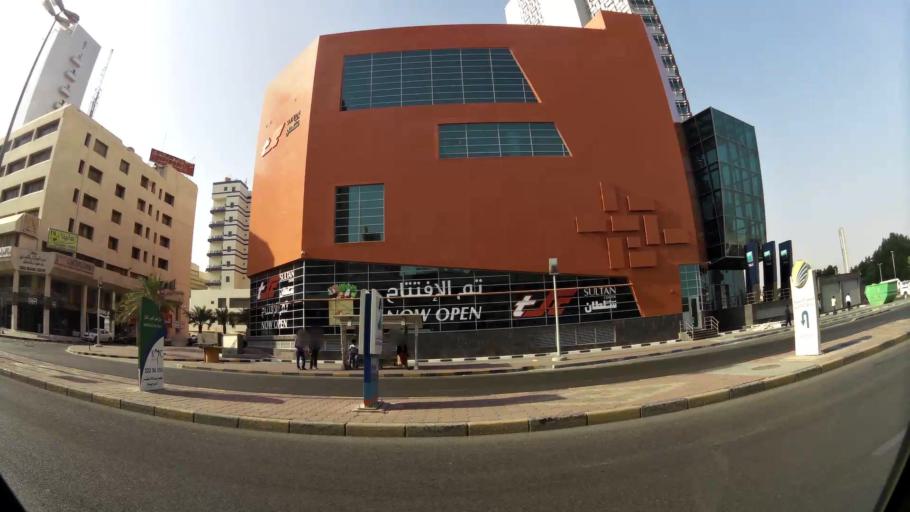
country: KW
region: Al Asimah
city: Ad Dasmah
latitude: 29.3472
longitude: 48.0129
